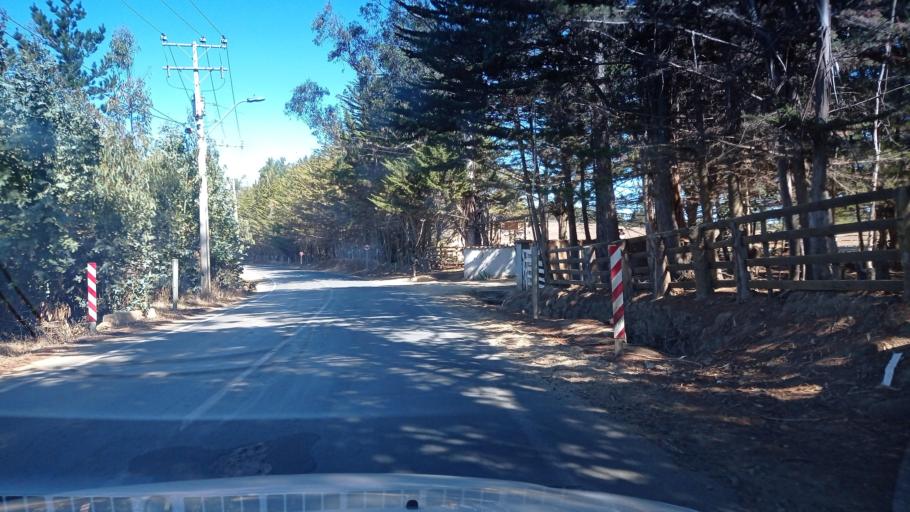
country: CL
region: O'Higgins
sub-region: Provincia de Colchagua
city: Santa Cruz
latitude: -34.4163
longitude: -71.9999
